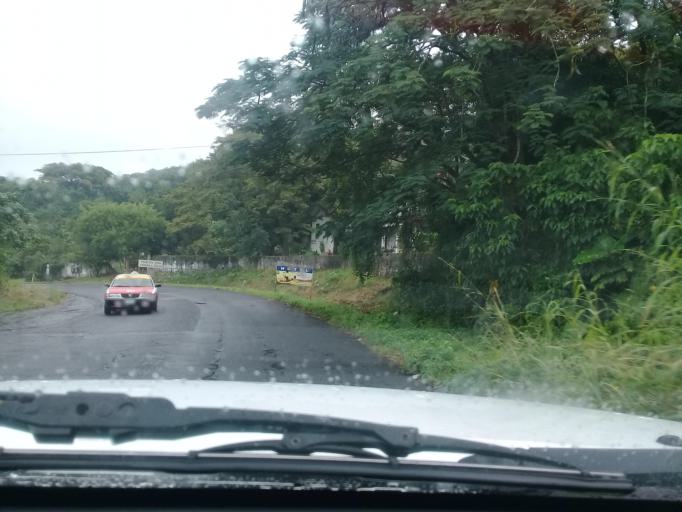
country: MX
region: Veracruz
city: Santiago Tuxtla
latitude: 18.4619
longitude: -95.2950
